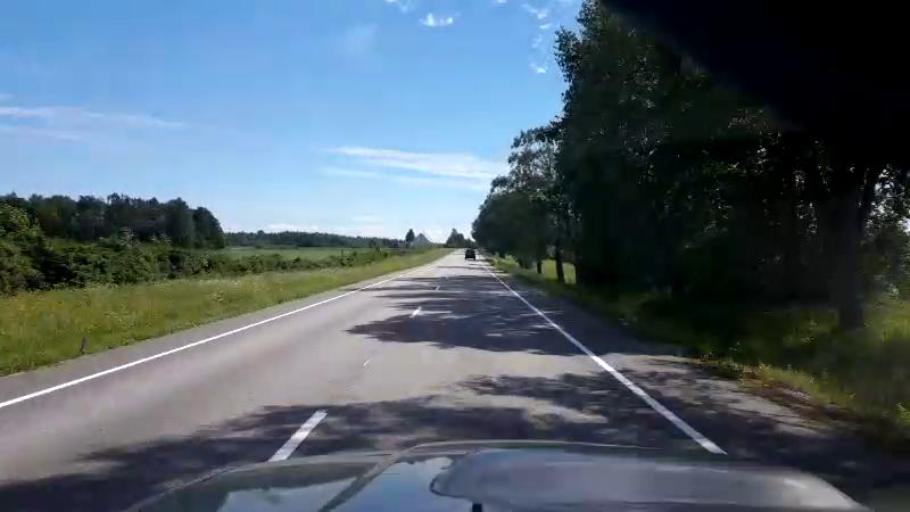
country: EE
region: Jaervamaa
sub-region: Jaerva-Jaani vald
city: Jarva-Jaani
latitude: 59.0077
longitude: 25.9272
